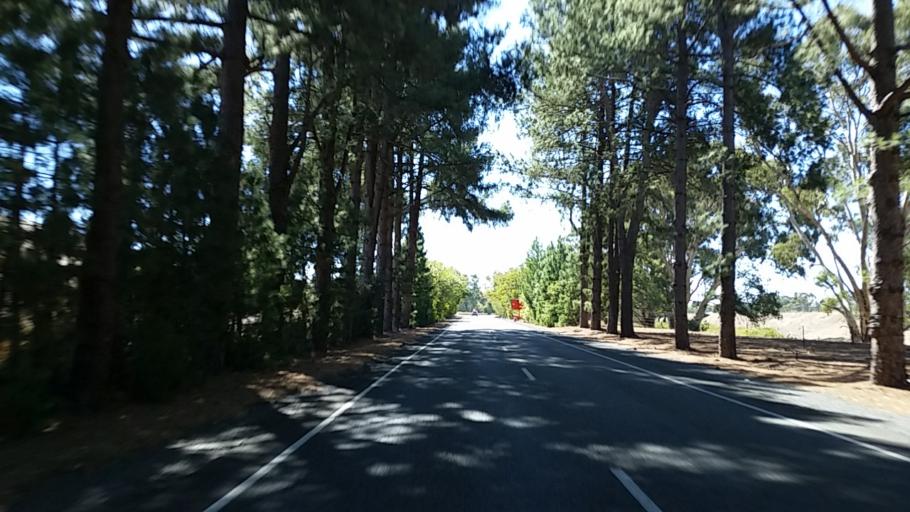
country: AU
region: South Australia
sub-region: Light
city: Kapunda
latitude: -34.0911
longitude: 138.7753
